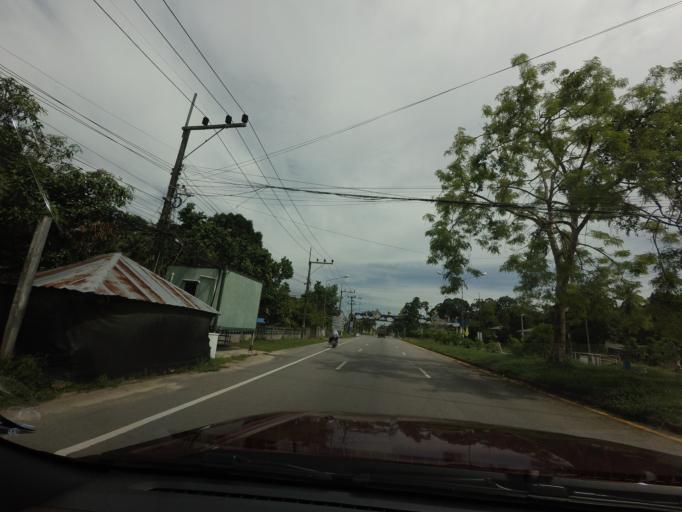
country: TH
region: Narathiwat
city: Tak Bai
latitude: 6.2597
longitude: 102.0440
